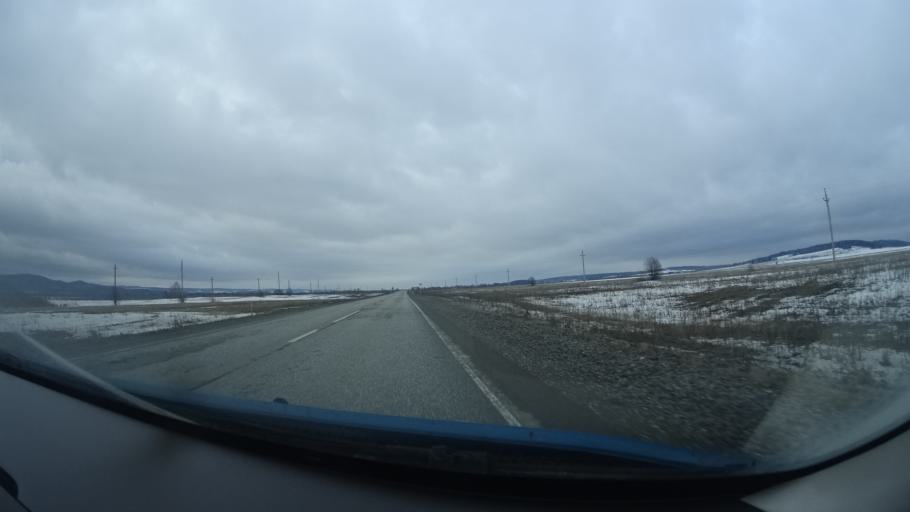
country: RU
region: Perm
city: Barda
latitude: 56.9815
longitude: 55.5764
